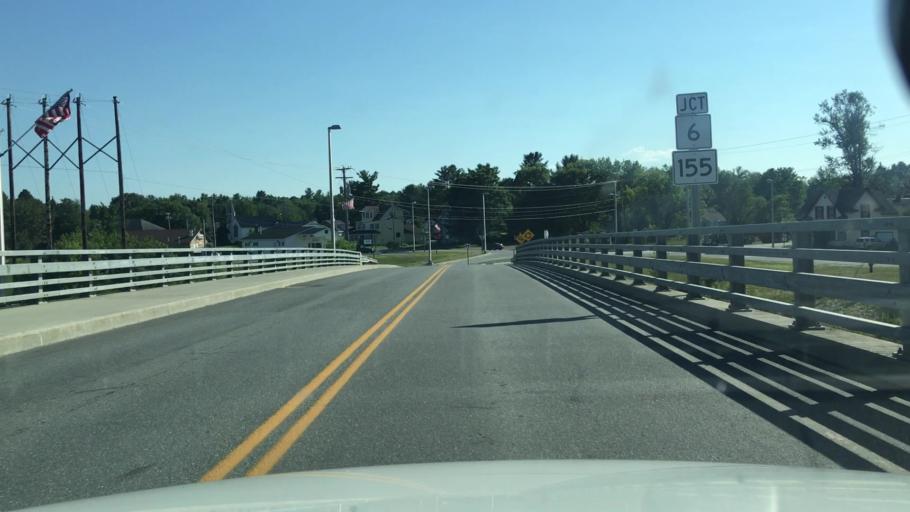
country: US
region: Maine
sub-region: Penobscot County
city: Howland
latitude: 45.2394
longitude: -68.6590
